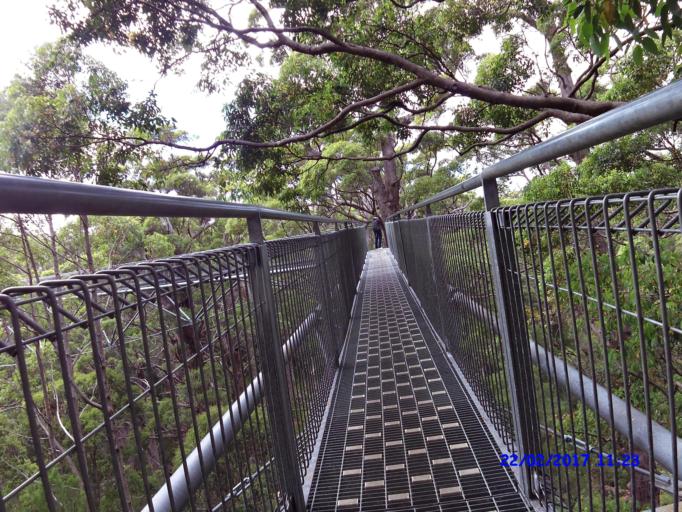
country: AU
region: Western Australia
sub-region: Denmark
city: Denmark
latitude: -34.9768
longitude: 116.8943
